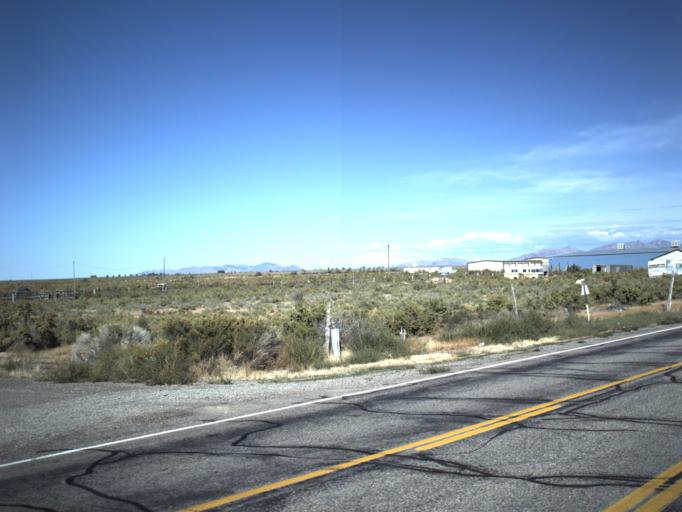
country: US
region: Utah
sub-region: Millard County
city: Delta
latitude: 39.3526
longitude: -112.5505
